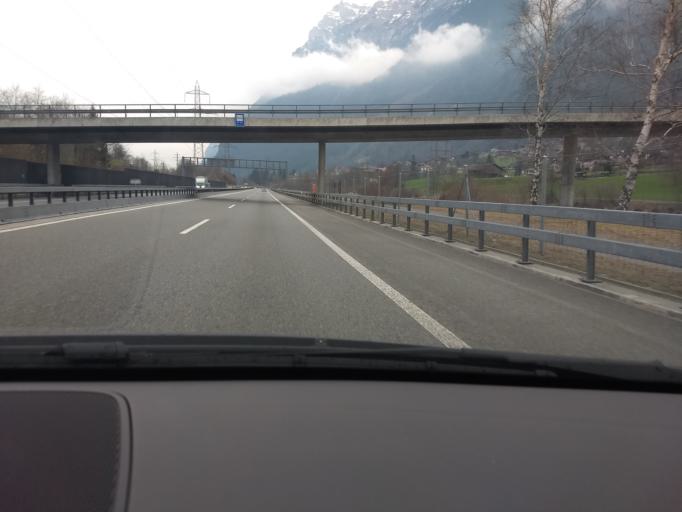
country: CH
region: Uri
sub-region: Uri
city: Silenen
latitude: 46.7942
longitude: 8.6652
